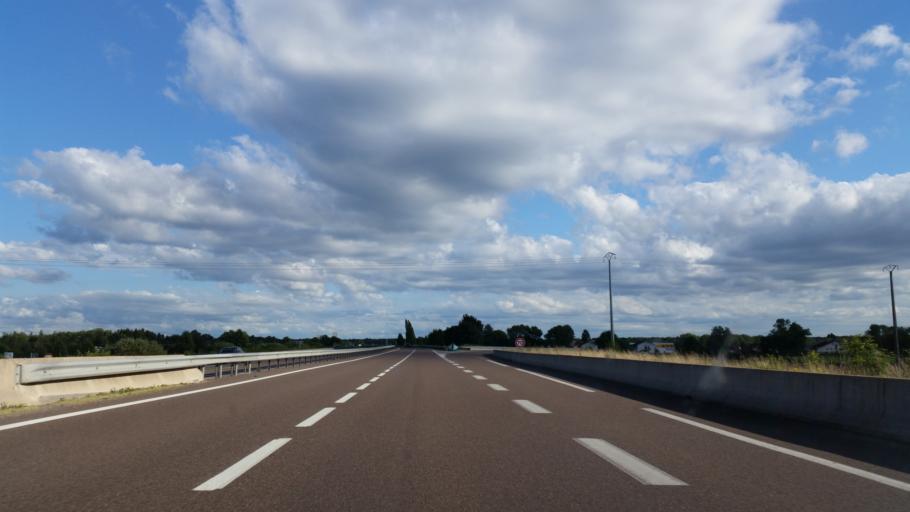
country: FR
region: Franche-Comte
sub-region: Departement de la Haute-Saone
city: Lure
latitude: 47.6789
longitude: 6.5174
